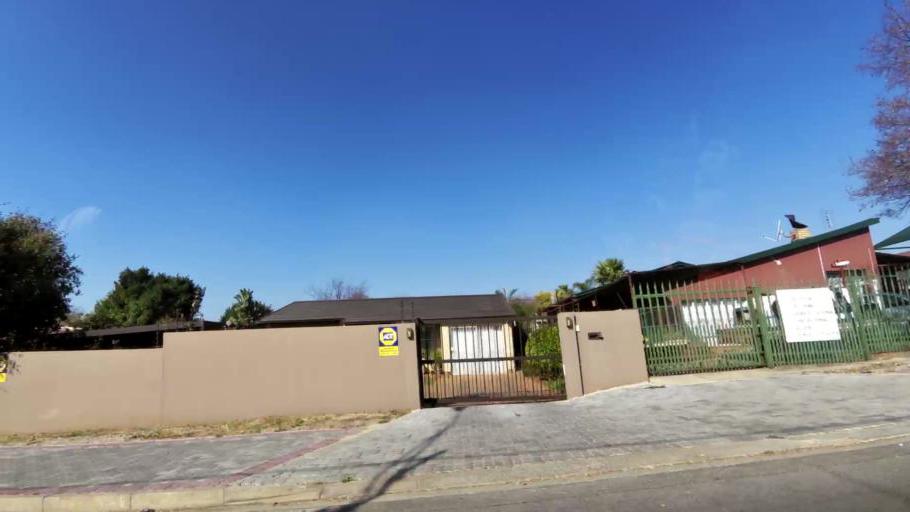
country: ZA
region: Gauteng
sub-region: City of Johannesburg Metropolitan Municipality
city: Johannesburg
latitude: -26.1743
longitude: 27.9848
